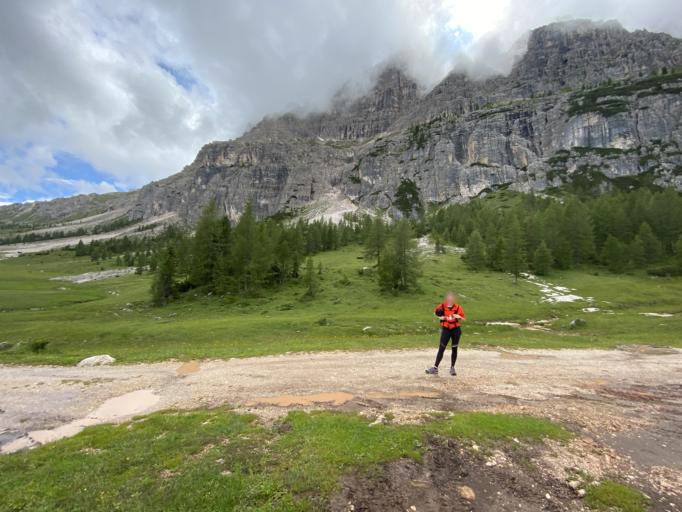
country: IT
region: Veneto
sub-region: Provincia di Belluno
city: Cortina d'Ampezzo
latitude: 46.4855
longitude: 12.1066
